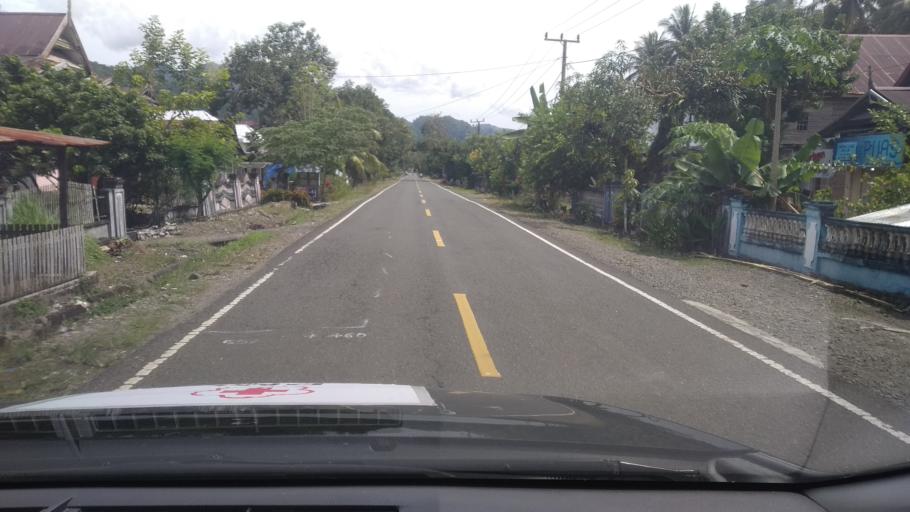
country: ID
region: Sulawesi Barat
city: Tapalang
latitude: -2.8836
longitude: 118.8850
